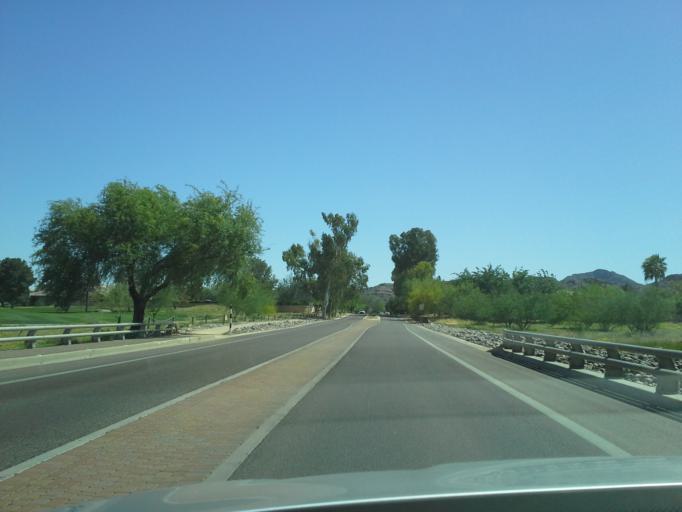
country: US
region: Arizona
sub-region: Maricopa County
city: Paradise Valley
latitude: 33.5628
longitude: -111.9434
